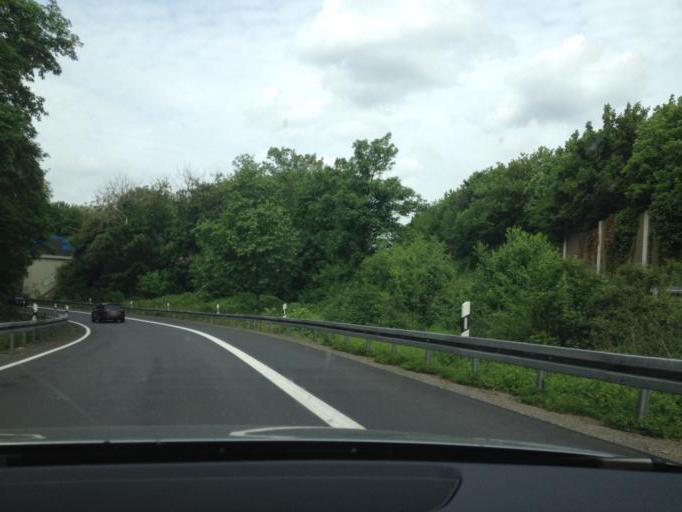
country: DE
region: North Rhine-Westphalia
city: Meiderich
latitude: 51.4838
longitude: 6.7724
